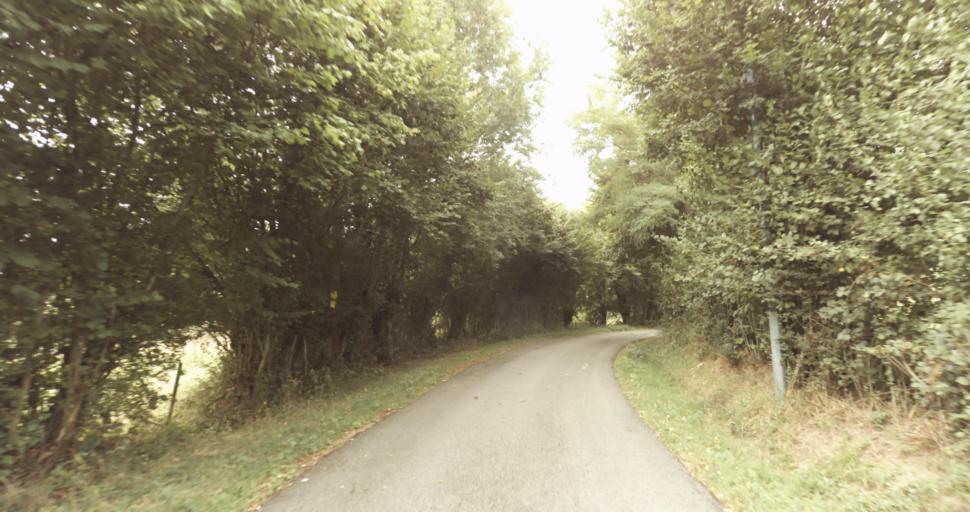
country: FR
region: Lower Normandy
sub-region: Departement de l'Orne
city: Gace
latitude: 48.7796
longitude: 0.3666
